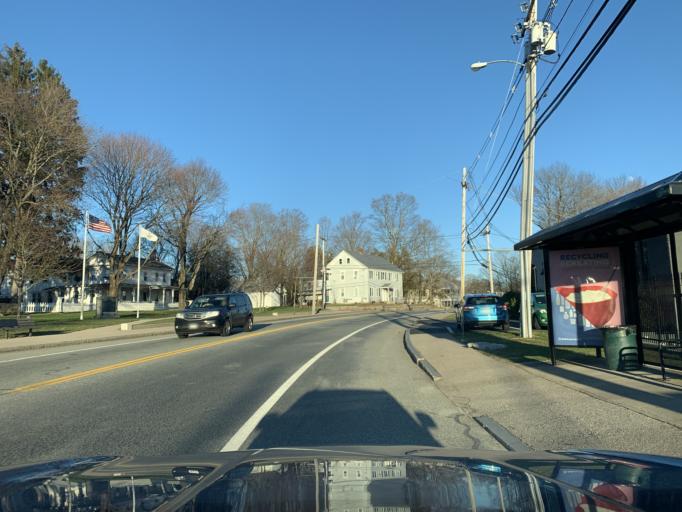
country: US
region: Rhode Island
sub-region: Kent County
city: West Warwick
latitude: 41.6968
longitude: -71.5471
